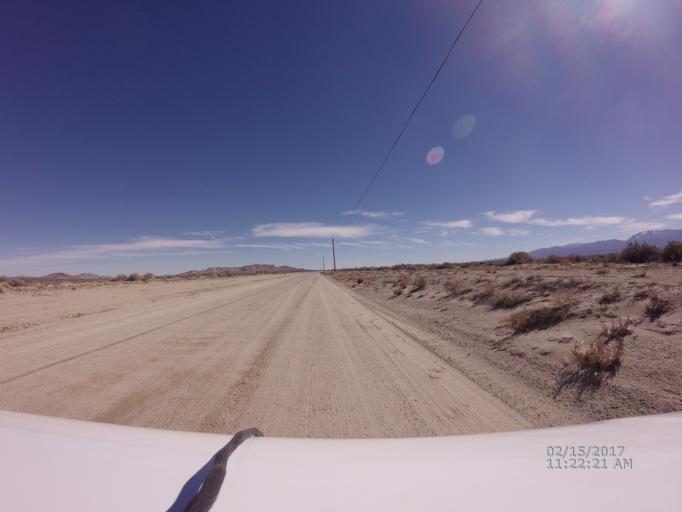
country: US
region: California
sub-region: Los Angeles County
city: Littlerock
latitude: 34.5870
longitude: -117.9196
